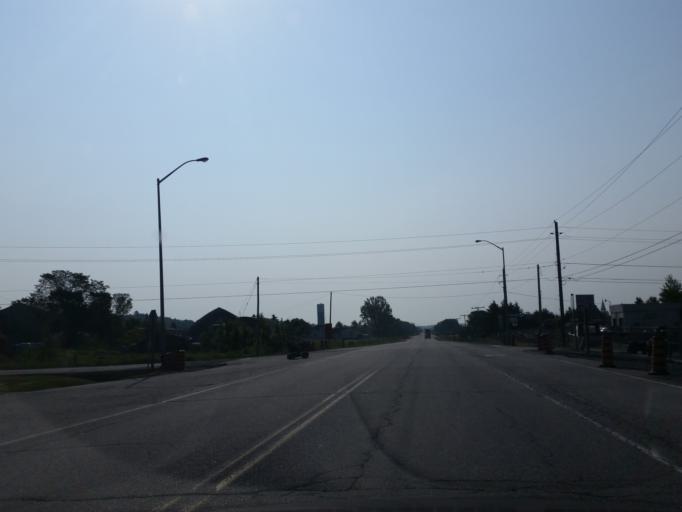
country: CA
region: Ontario
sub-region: Nipissing District
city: North Bay
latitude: 46.4147
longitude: -80.1344
